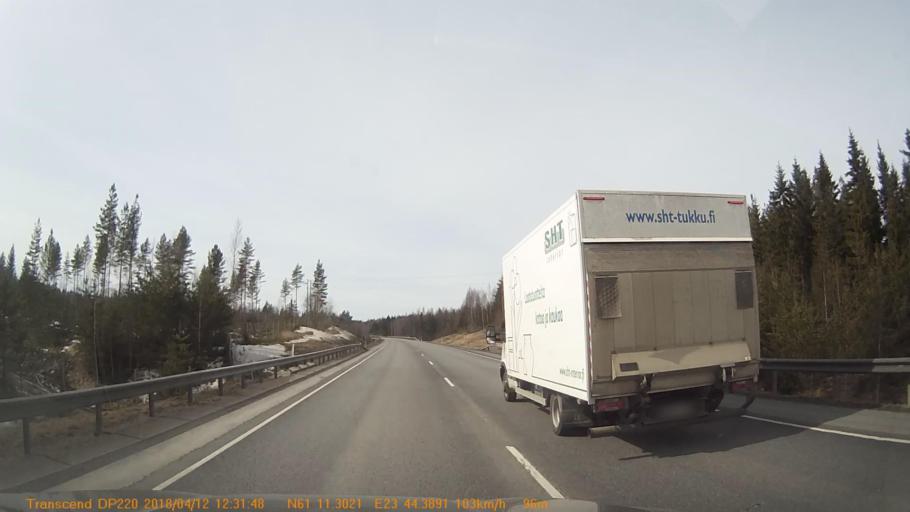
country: FI
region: Pirkanmaa
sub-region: Etelae-Pirkanmaa
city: Viiala
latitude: 61.1884
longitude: 23.7390
